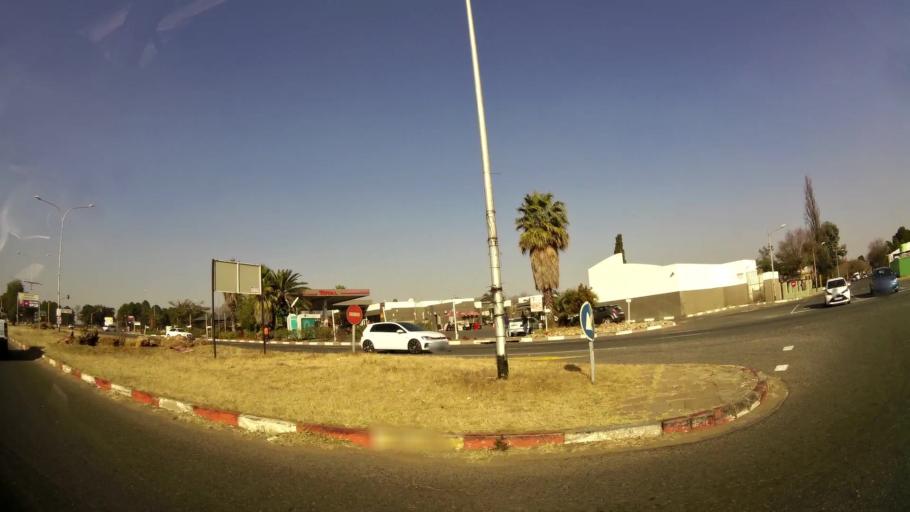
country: ZA
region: Gauteng
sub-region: West Rand District Municipality
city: Randfontein
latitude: -26.1745
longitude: 27.7067
